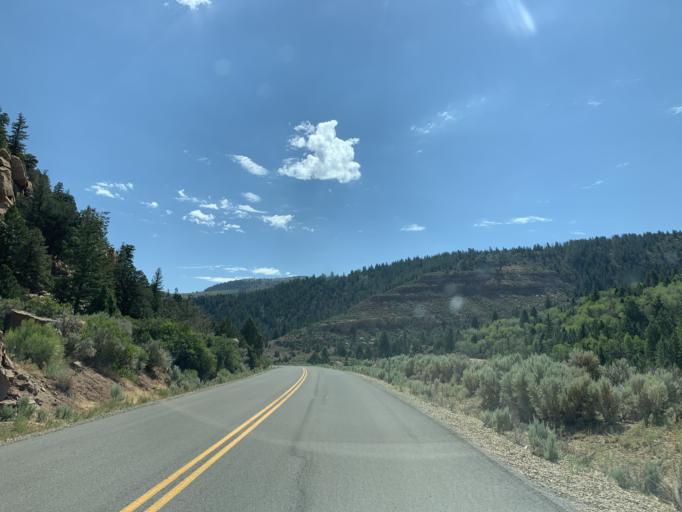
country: US
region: Utah
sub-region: Carbon County
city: East Carbon City
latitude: 39.7545
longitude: -110.5375
